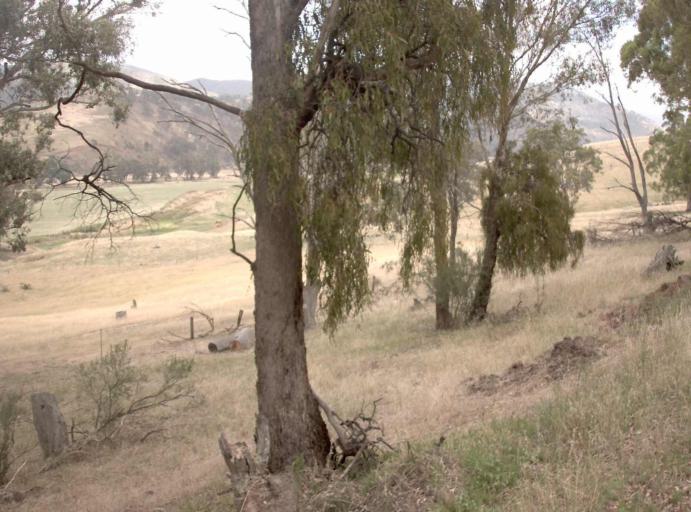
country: AU
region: Victoria
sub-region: Wellington
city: Heyfield
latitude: -37.6806
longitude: 146.6558
